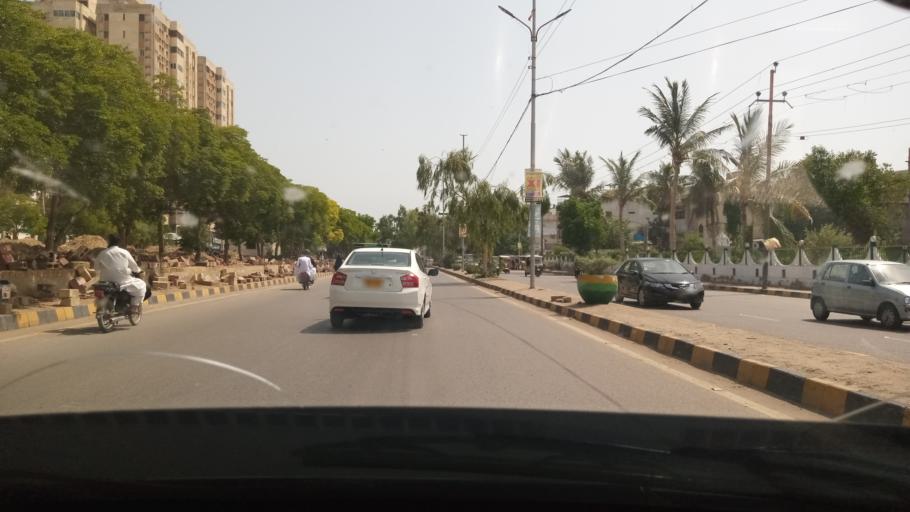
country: PK
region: Sindh
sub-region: Karachi District
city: Karachi
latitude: 24.8725
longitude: 67.0486
